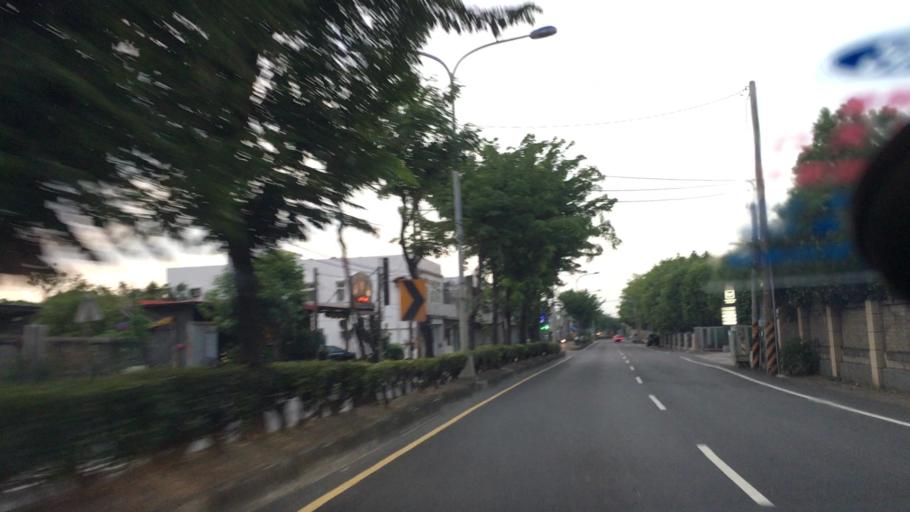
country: TW
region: Taiwan
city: Taoyuan City
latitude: 25.0575
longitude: 121.2681
